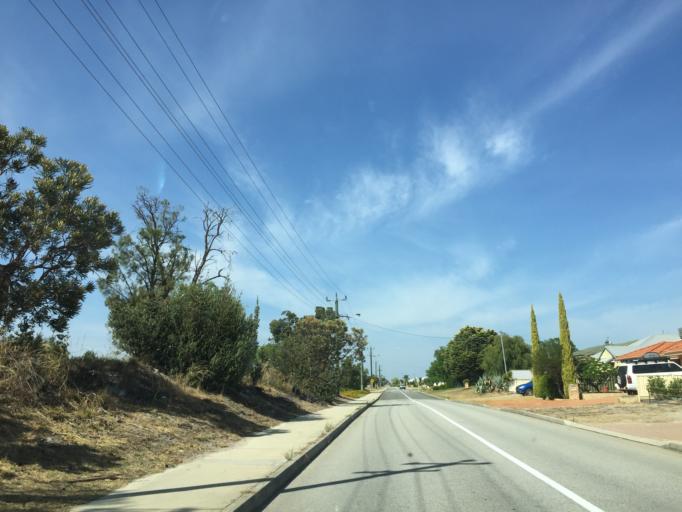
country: AU
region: Western Australia
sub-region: Gosnells
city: Thornlie
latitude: -32.0827
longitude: 115.9597
